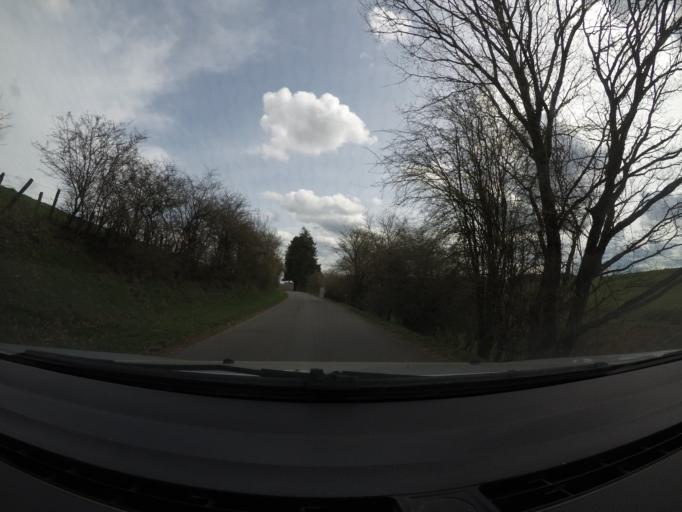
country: BE
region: Wallonia
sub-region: Province du Luxembourg
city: Neufchateau
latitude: 49.8199
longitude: 5.4669
